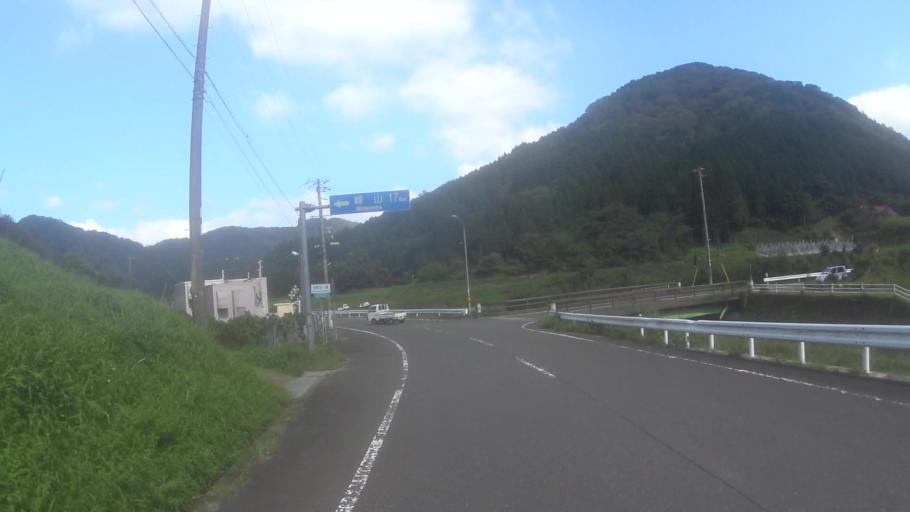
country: JP
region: Kyoto
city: Miyazu
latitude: 35.6803
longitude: 135.1586
